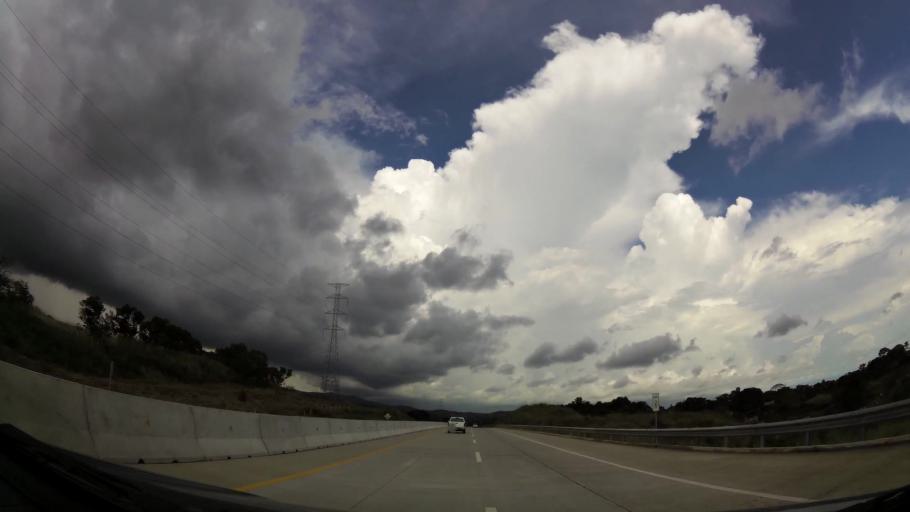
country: PA
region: Panama
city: Tocumen
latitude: 9.0989
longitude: -79.4190
